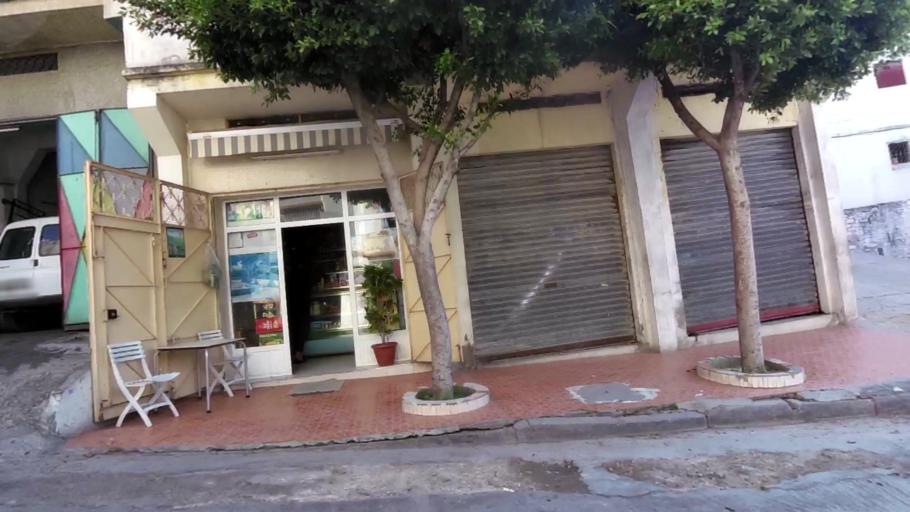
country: MA
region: Tanger-Tetouan
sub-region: Tanger-Assilah
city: Tangier
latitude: 35.7624
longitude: -5.7911
